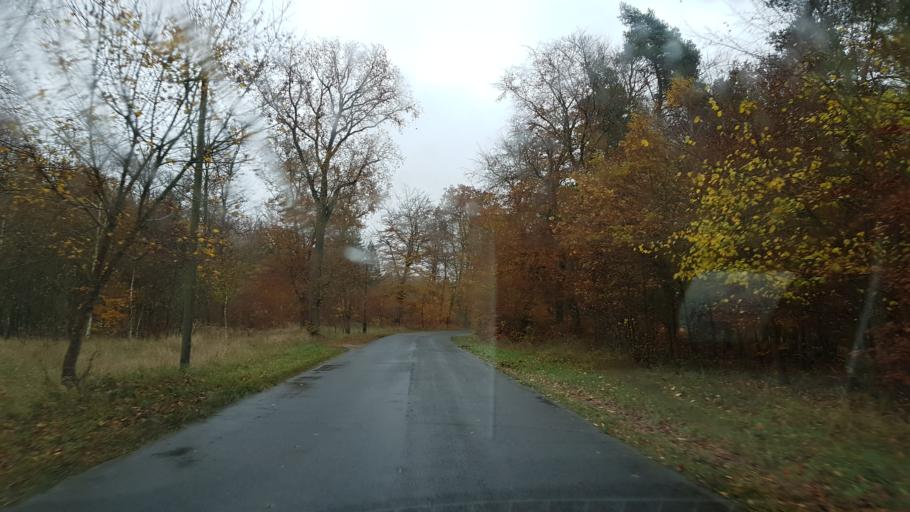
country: PL
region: West Pomeranian Voivodeship
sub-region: Powiat goleniowski
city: Stepnica
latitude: 53.6573
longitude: 14.6649
